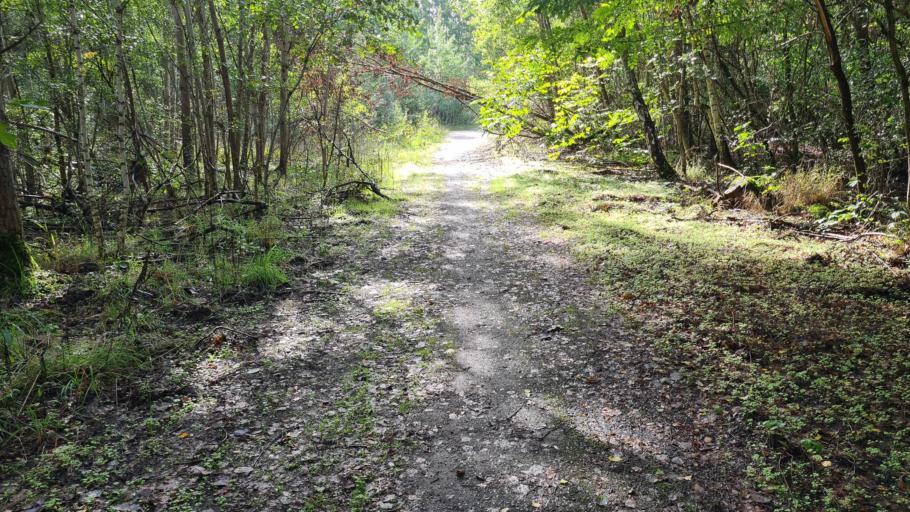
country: DE
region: Brandenburg
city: Sallgast
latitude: 51.5624
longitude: 13.8582
